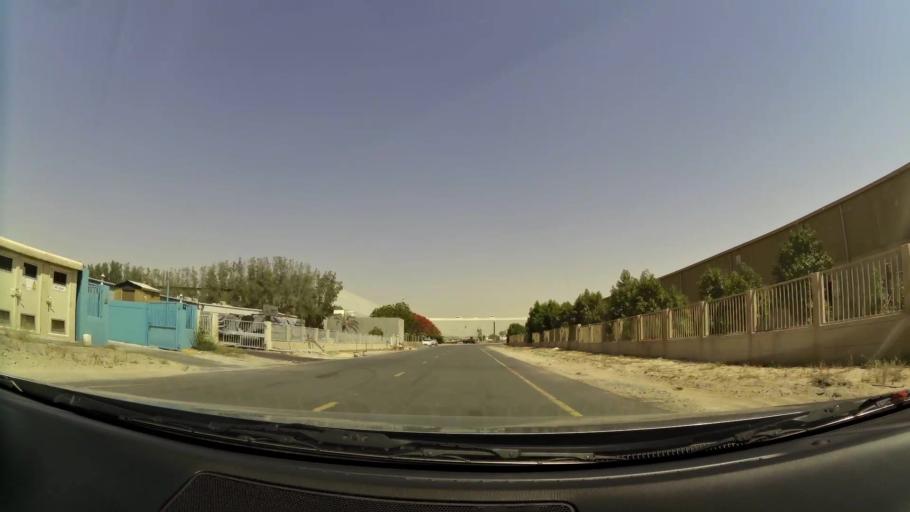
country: AE
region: Dubai
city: Dubai
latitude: 24.9876
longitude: 55.1595
